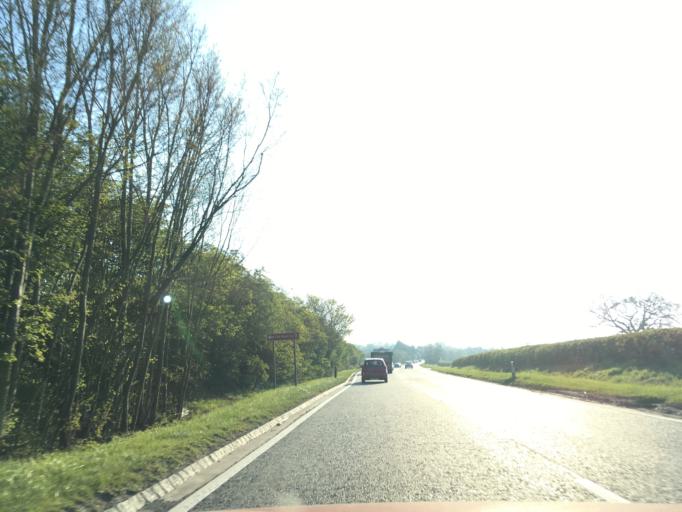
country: GB
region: England
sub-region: Oxfordshire
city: North Leigh
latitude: 51.7911
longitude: -1.4229
